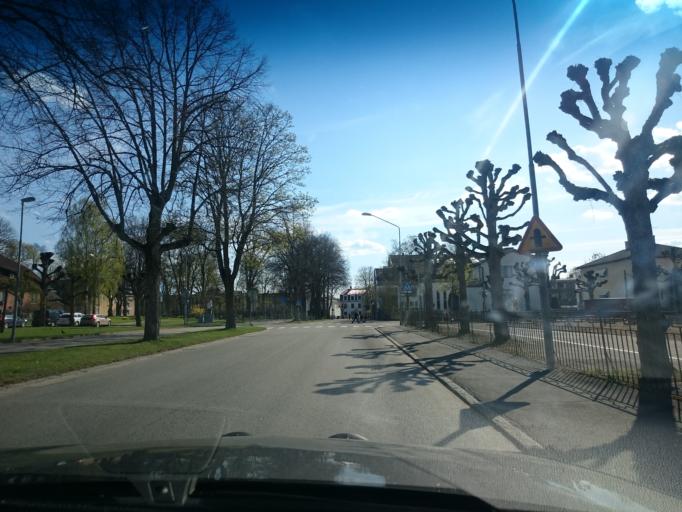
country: SE
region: Joenkoeping
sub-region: Vetlanda Kommun
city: Vetlanda
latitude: 57.4290
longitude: 15.0823
